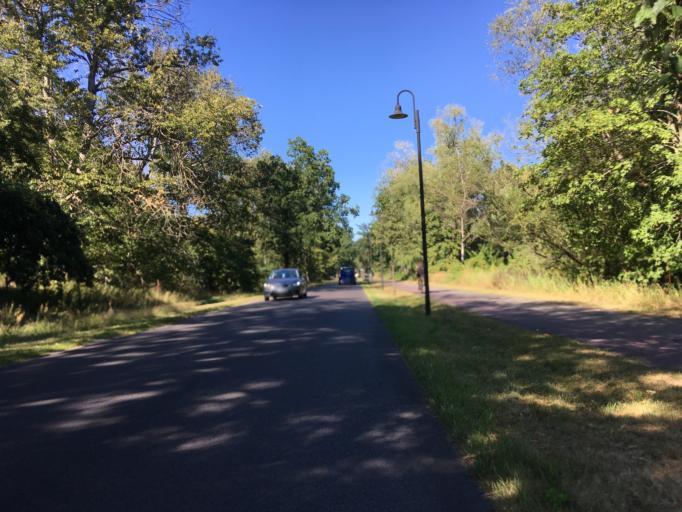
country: DE
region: Brandenburg
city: Schulzendorf
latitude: 52.3649
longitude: 13.5916
